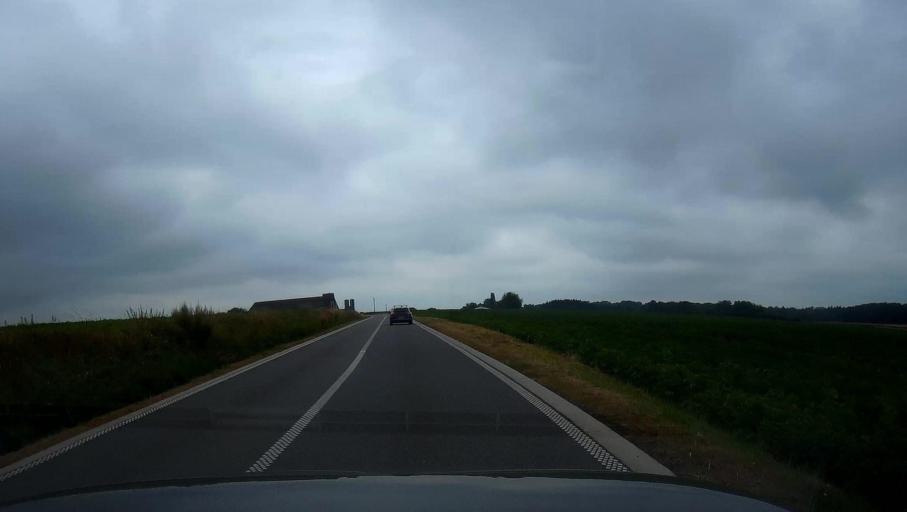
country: BE
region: Wallonia
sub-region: Province de Namur
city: Assesse
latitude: 50.3487
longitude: 5.0405
